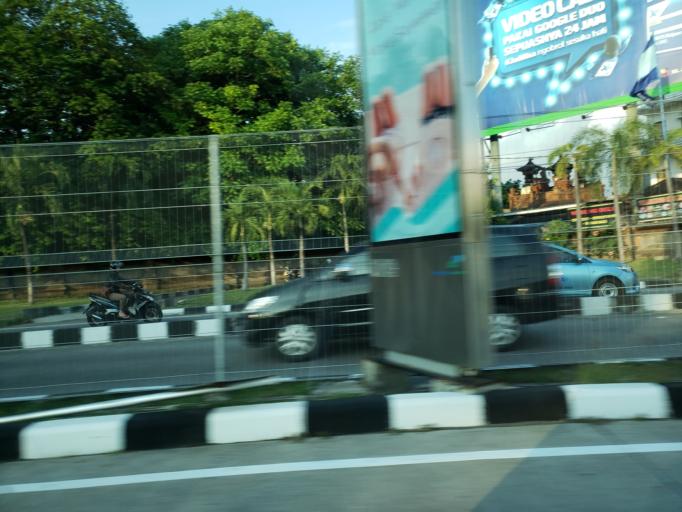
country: ID
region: Bali
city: Kelanabian
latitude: -8.7408
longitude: 115.1680
